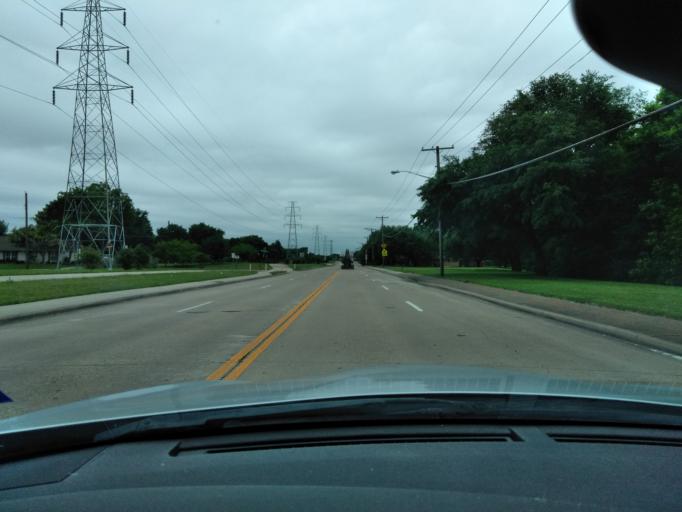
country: US
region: Texas
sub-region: Dallas County
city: Richardson
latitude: 32.9584
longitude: -96.7786
